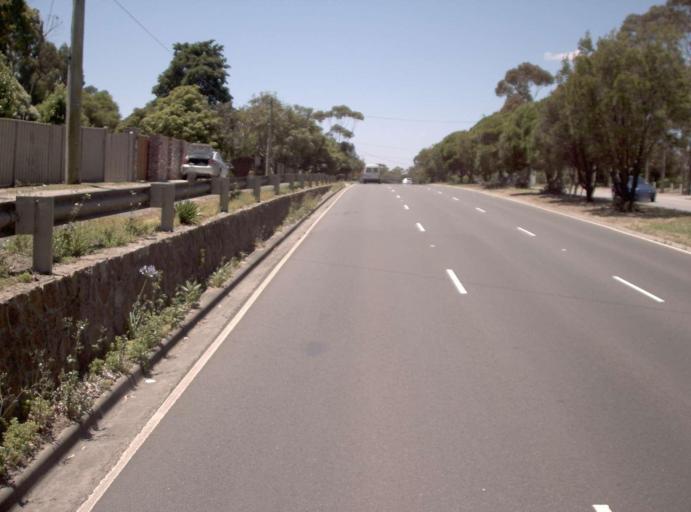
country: AU
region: Victoria
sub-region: Mornington Peninsula
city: Mount Eliza
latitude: -38.1973
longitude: 145.0872
